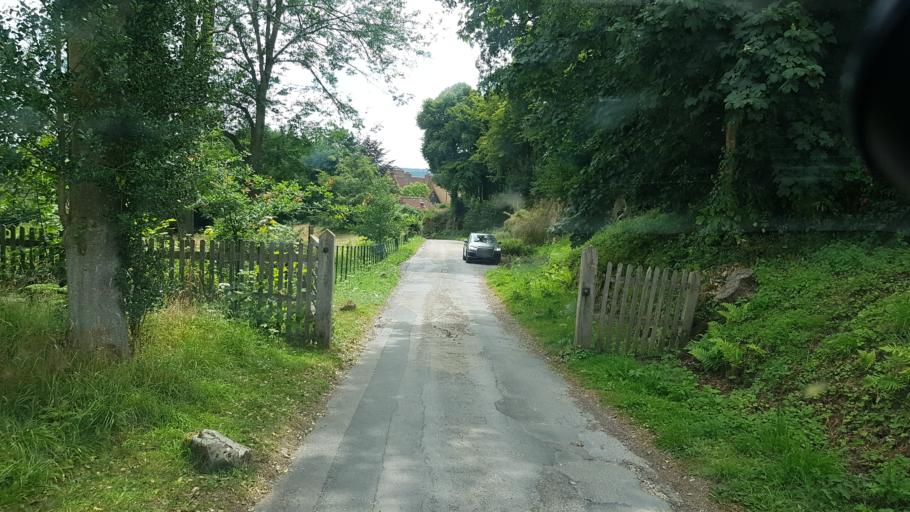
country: GB
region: England
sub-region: West Sussex
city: East Grinstead
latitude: 51.1044
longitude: -0.0185
